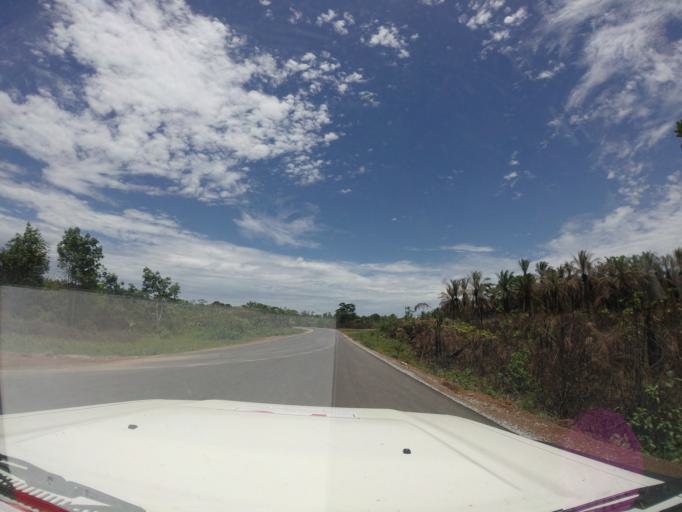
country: LR
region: Margibi
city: Kakata
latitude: 6.8017
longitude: -9.9460
